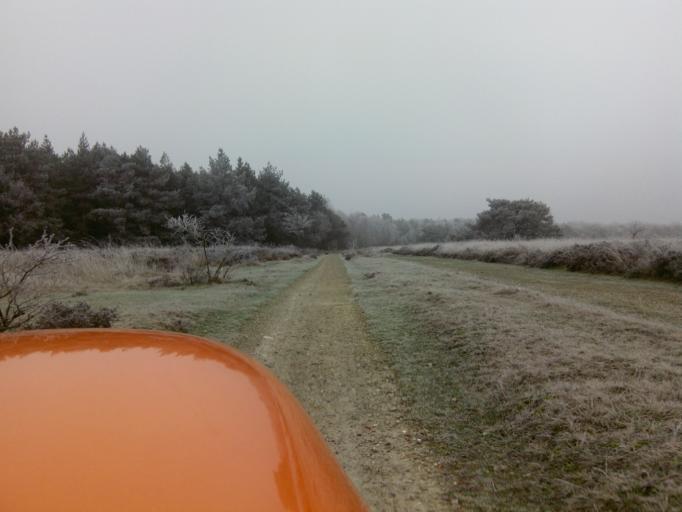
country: NL
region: Gelderland
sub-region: Gemeente Barneveld
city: Garderen
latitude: 52.2540
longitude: 5.7432
